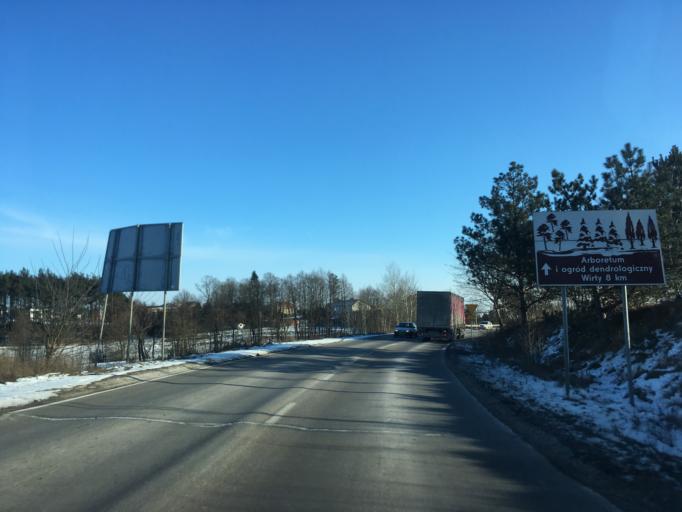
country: PL
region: Pomeranian Voivodeship
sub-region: Powiat starogardzki
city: Zblewo
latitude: 53.9350
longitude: 18.3341
